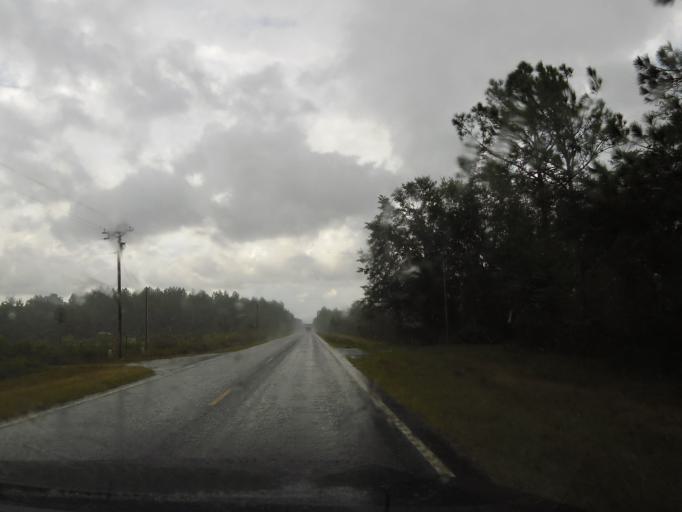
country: US
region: Florida
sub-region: Nassau County
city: Hilliard
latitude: 30.5363
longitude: -82.0394
